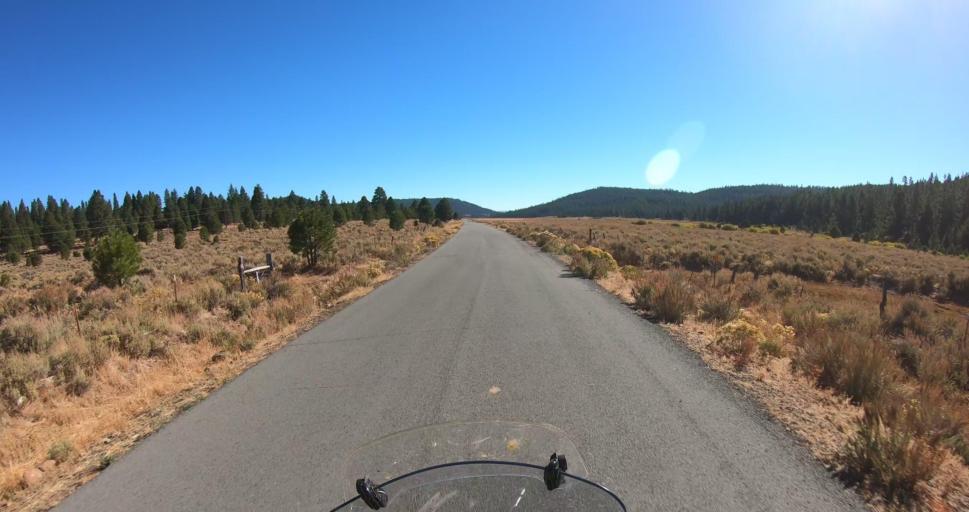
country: US
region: Oregon
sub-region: Lake County
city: Lakeview
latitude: 42.2139
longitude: -120.2469
